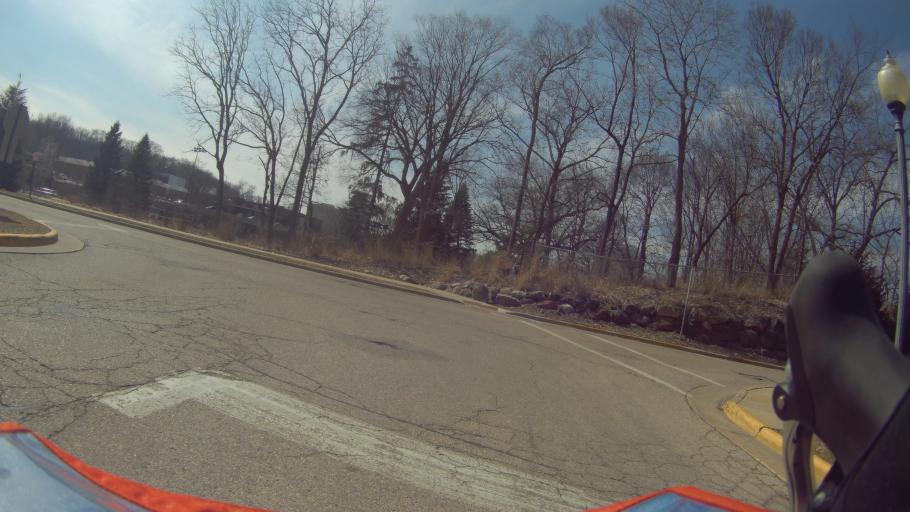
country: US
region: Wisconsin
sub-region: Dane County
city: Shorewood Hills
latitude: 43.0758
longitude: -89.4385
